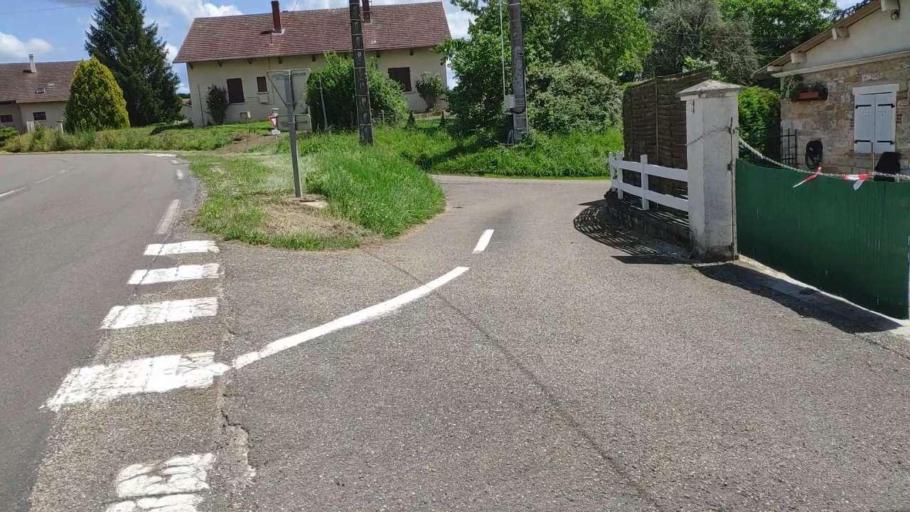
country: FR
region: Franche-Comte
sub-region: Departement du Jura
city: Chaussin
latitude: 46.8628
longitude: 5.4540
